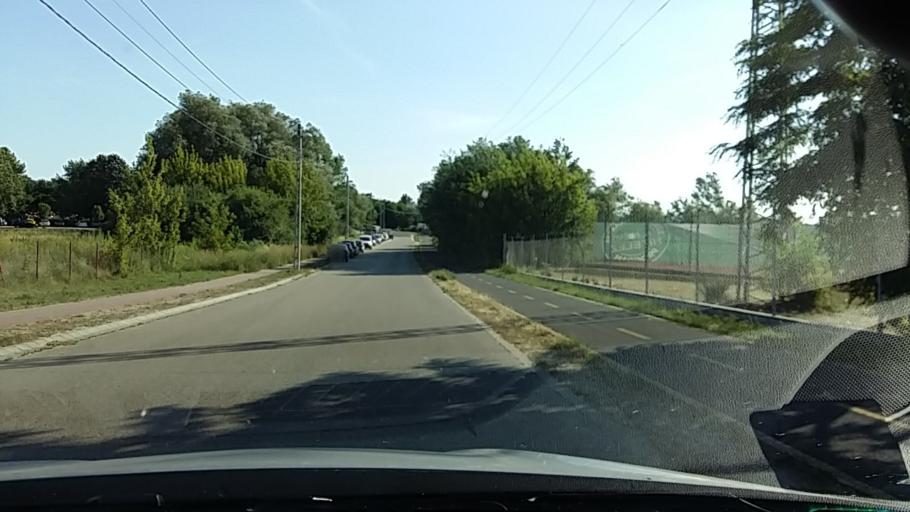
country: HU
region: Pest
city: God
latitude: 47.6940
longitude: 19.1514
